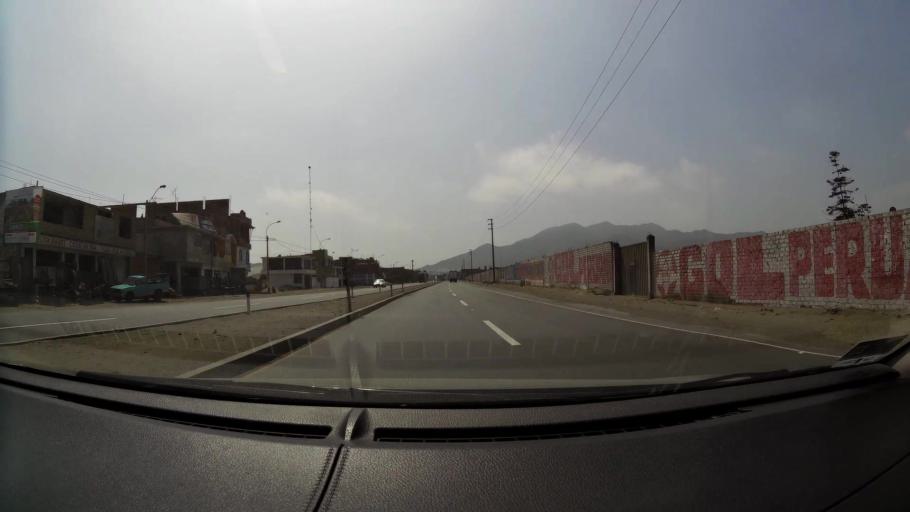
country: PE
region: Lima
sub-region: Provincia de Huaral
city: Chancay
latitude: -11.4935
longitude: -77.3037
